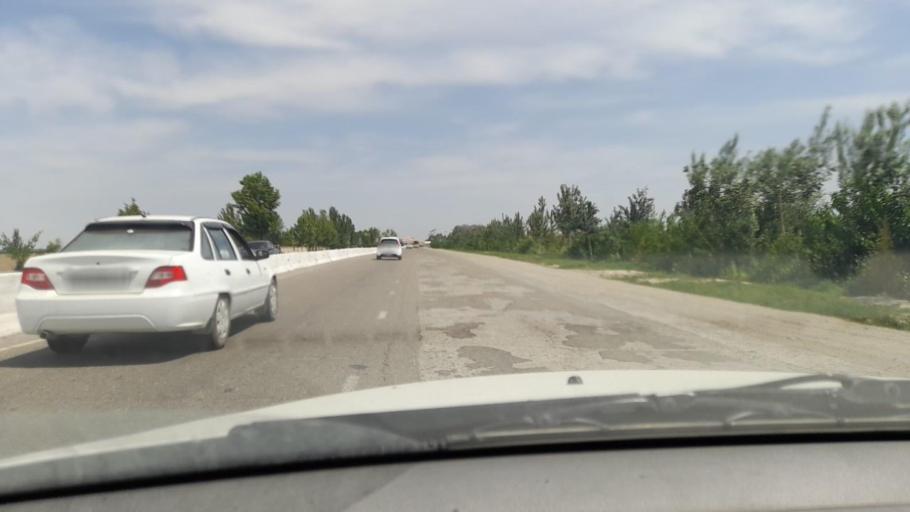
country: UZ
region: Bukhara
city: Wobkent
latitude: 40.0653
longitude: 64.5545
